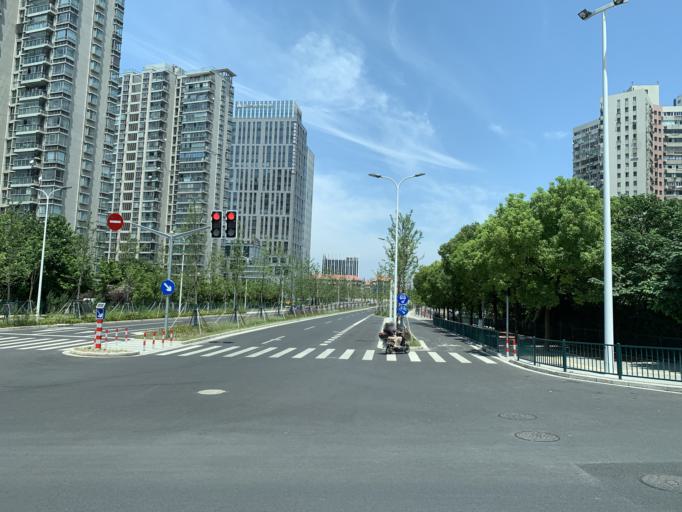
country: CN
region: Shanghai Shi
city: Pudong
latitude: 31.2472
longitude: 121.5449
